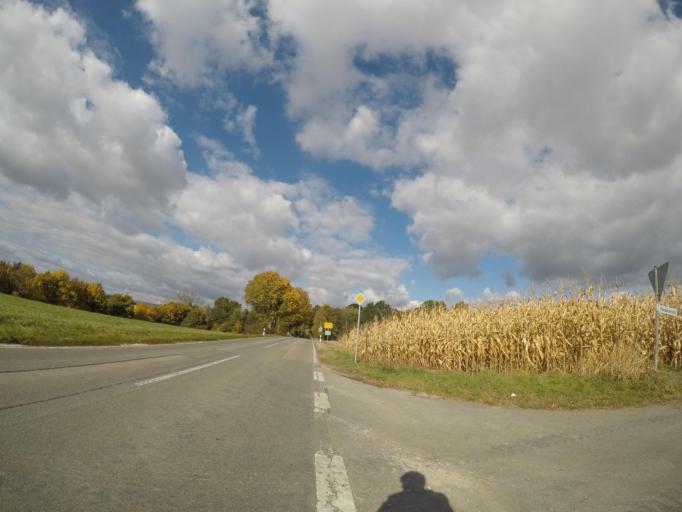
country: DE
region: Baden-Wuerttemberg
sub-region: Tuebingen Region
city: Oberstadion
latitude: 48.1825
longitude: 9.6908
